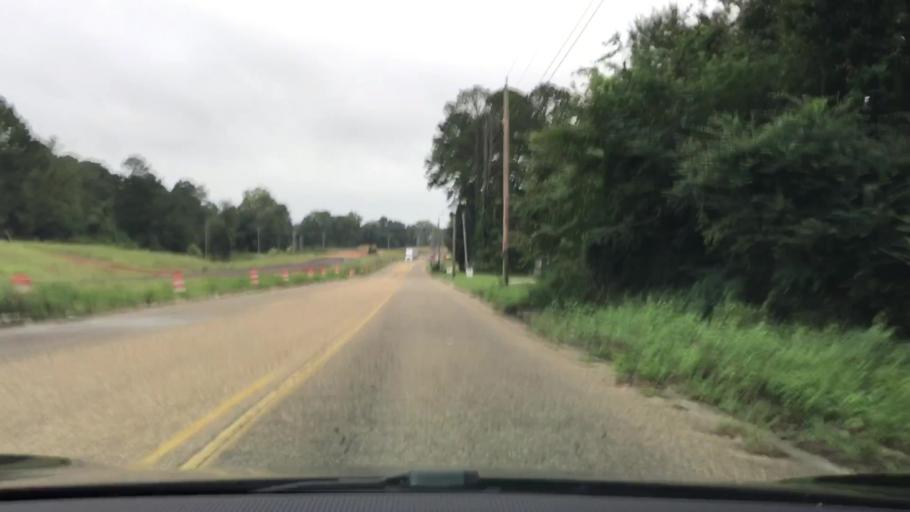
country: US
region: Alabama
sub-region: Coffee County
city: Elba
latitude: 31.4259
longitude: -86.0727
